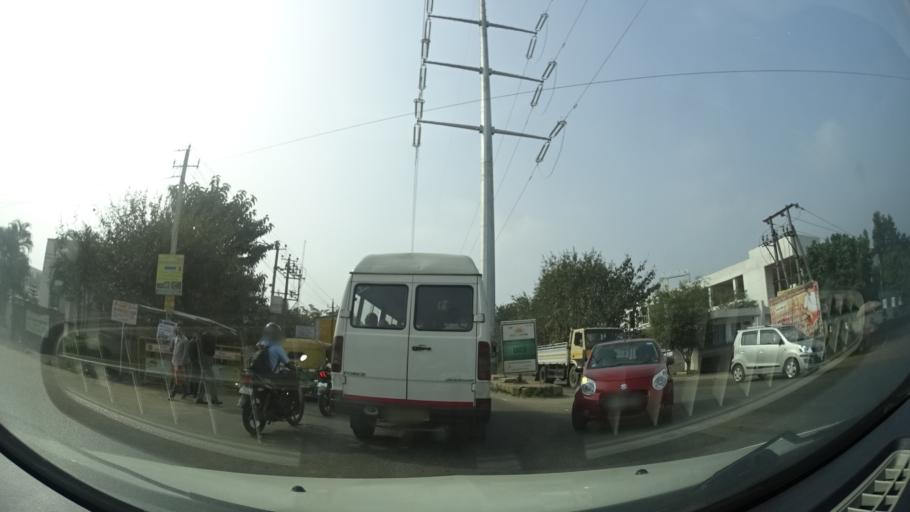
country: IN
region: Karnataka
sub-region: Bangalore Urban
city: Anekal
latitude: 12.7991
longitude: 77.6612
